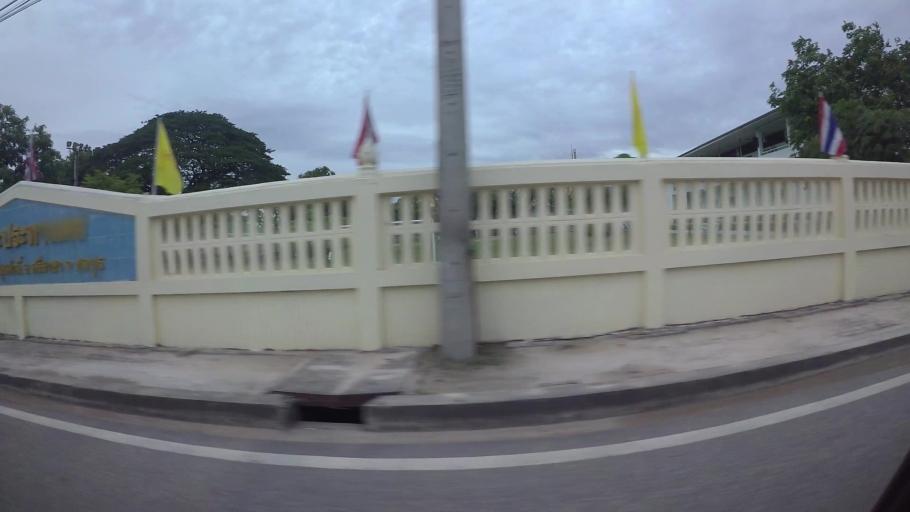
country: TH
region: Chon Buri
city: Si Racha
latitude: 13.1193
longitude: 100.9459
